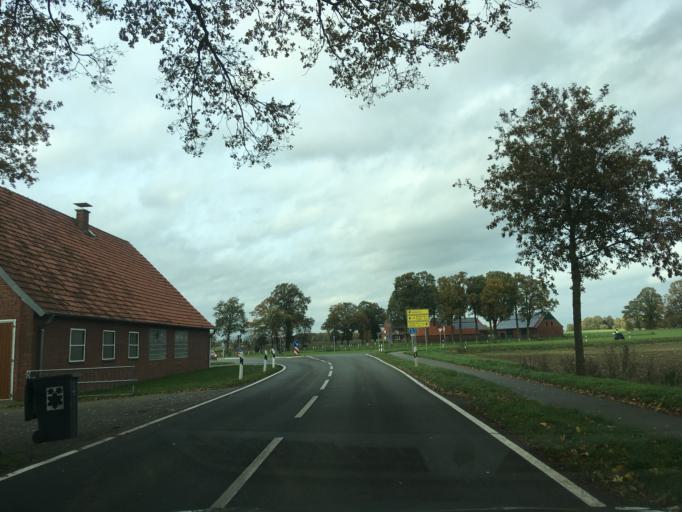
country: DE
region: North Rhine-Westphalia
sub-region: Regierungsbezirk Munster
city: Vreden
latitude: 52.0980
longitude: 6.8848
